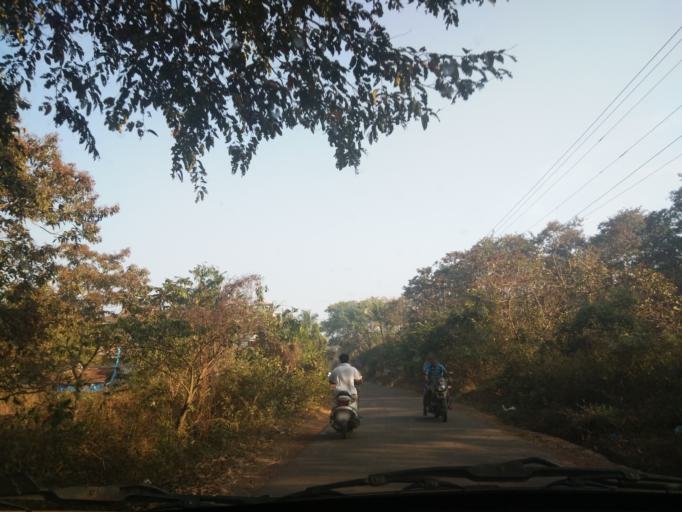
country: IN
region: Goa
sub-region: South Goa
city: Davorlim
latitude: 15.2830
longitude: 74.0067
